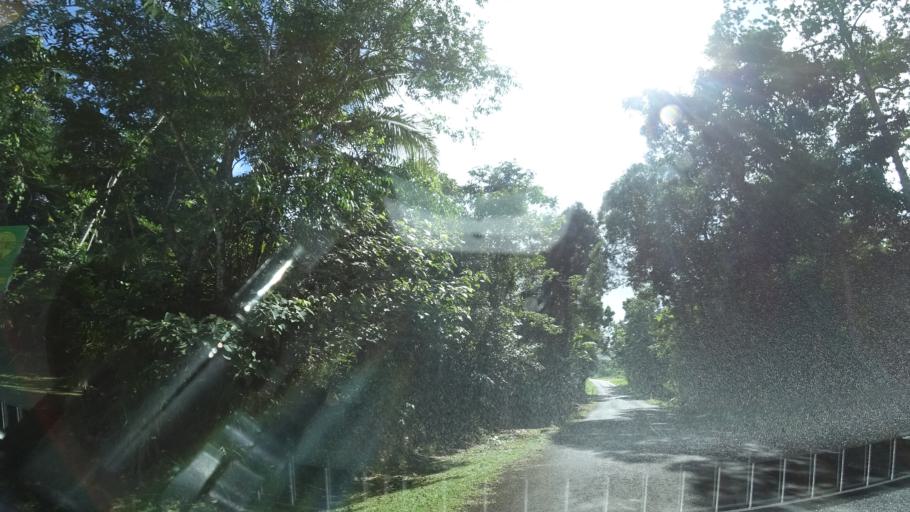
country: AU
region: Queensland
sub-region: Cairns
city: Port Douglas
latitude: -16.2012
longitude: 145.4117
